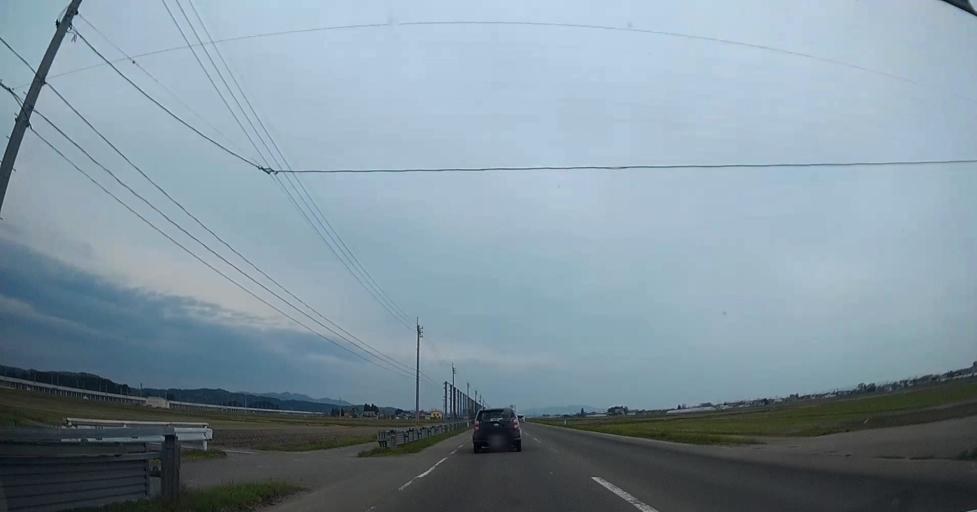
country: JP
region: Aomori
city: Aomori Shi
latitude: 40.8630
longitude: 140.6808
